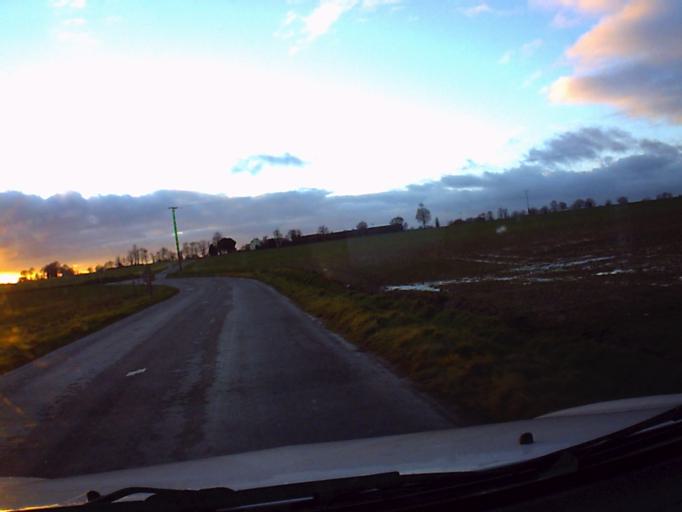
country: FR
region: Brittany
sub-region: Departement d'Ille-et-Vilaine
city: Iffendic
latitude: 48.1689
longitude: -1.9997
